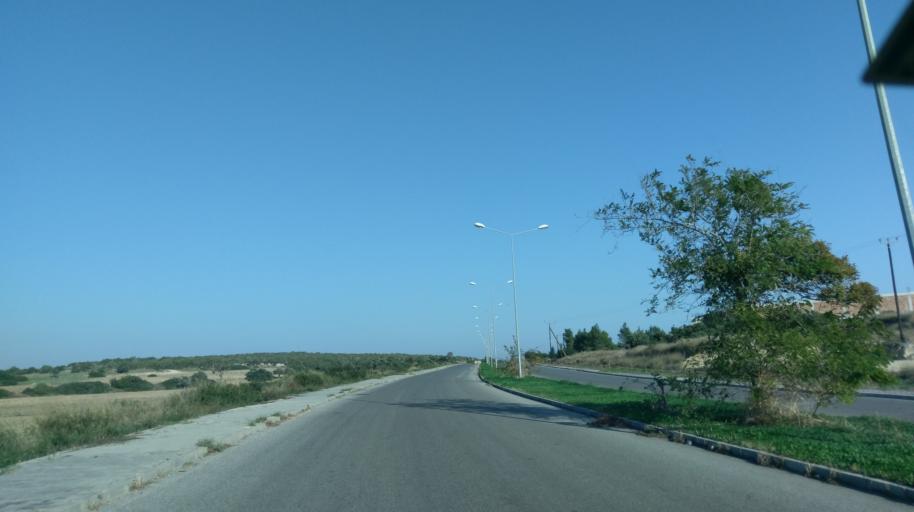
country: CY
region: Ammochostos
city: Leonarisso
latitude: 35.3710
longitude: 34.0769
